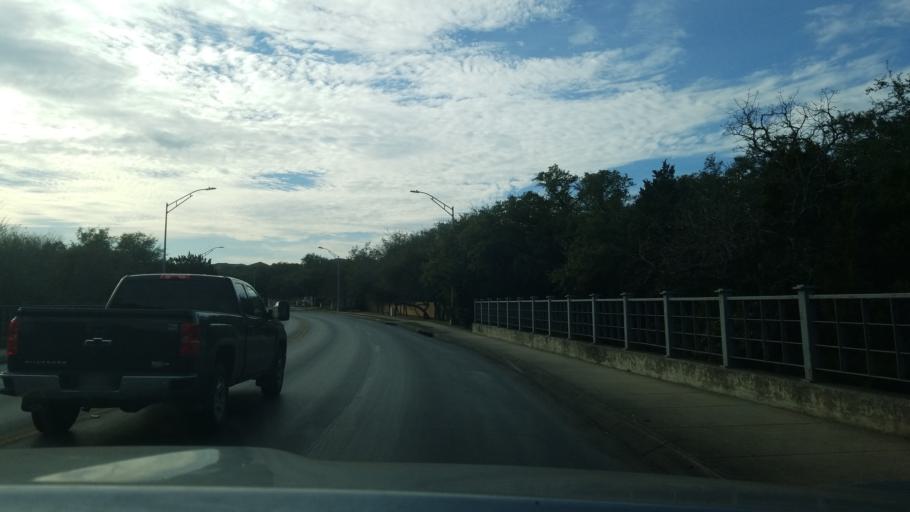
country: US
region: Texas
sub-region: Bexar County
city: Timberwood Park
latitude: 29.6866
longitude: -98.4629
